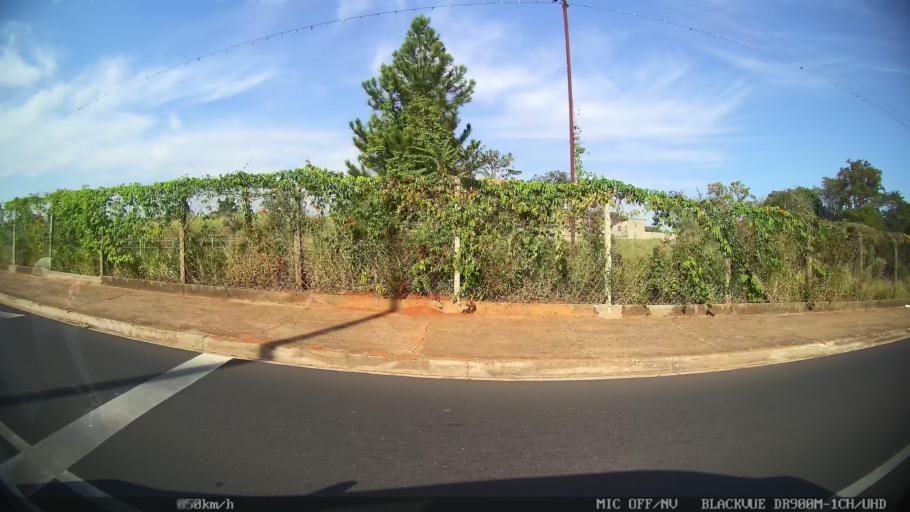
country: BR
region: Sao Paulo
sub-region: Araraquara
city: Araraquara
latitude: -21.7704
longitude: -48.1648
